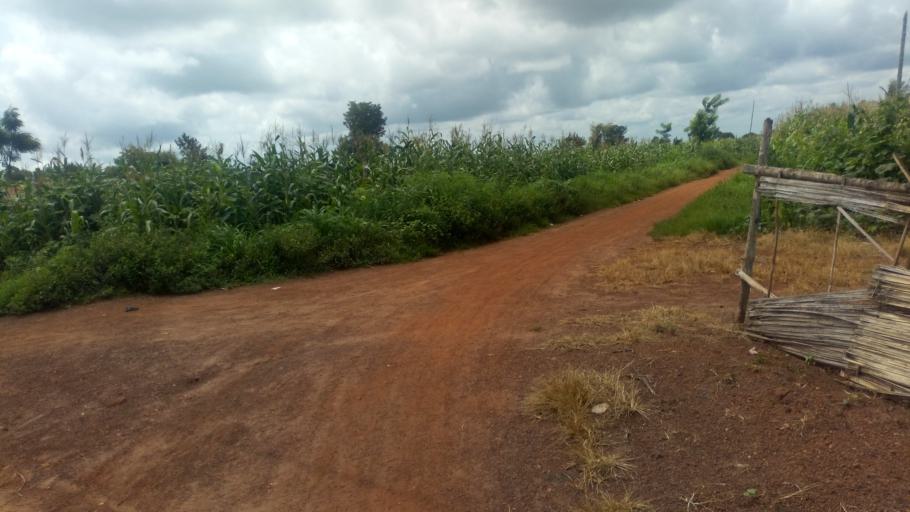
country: TG
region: Centrale
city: Sotouboua
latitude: 8.5553
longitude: 1.0034
